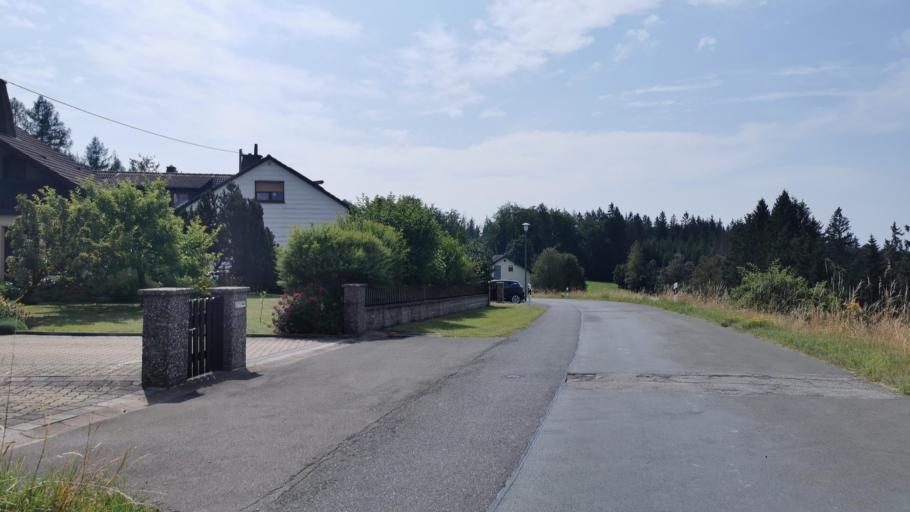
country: DE
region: Bavaria
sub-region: Upper Franconia
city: Wilhelmsthal
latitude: 50.2982
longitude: 11.3975
